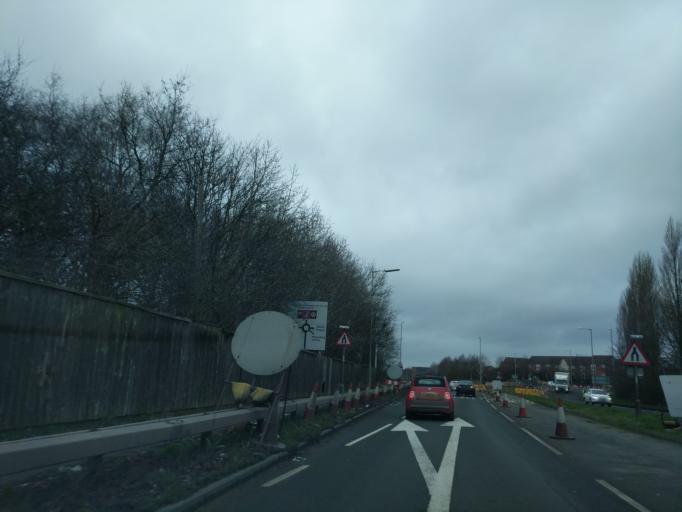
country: GB
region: England
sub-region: Staffordshire
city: Cannock
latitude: 52.6851
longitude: -2.0152
